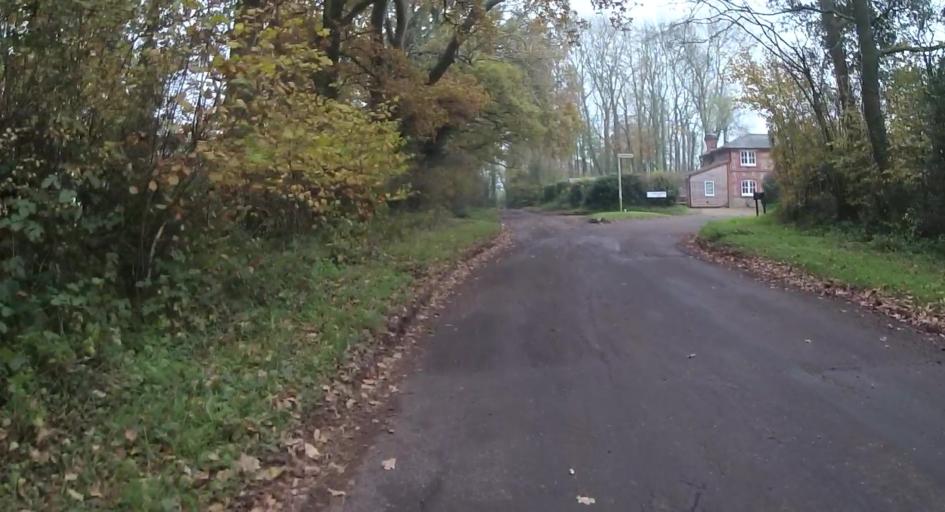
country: GB
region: England
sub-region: Hampshire
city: Old Basing
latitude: 51.2039
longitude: -1.0376
